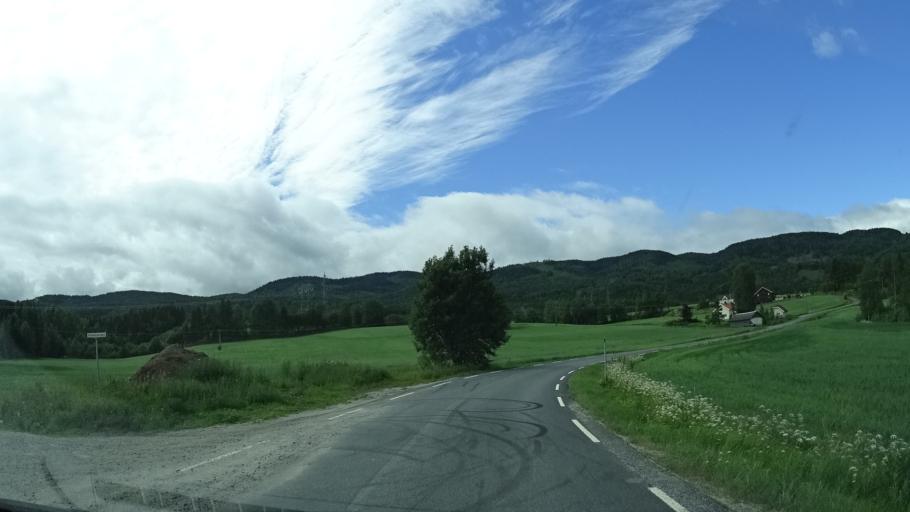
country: NO
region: Buskerud
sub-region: Modum
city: Vikersund
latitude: 60.2086
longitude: 9.9801
